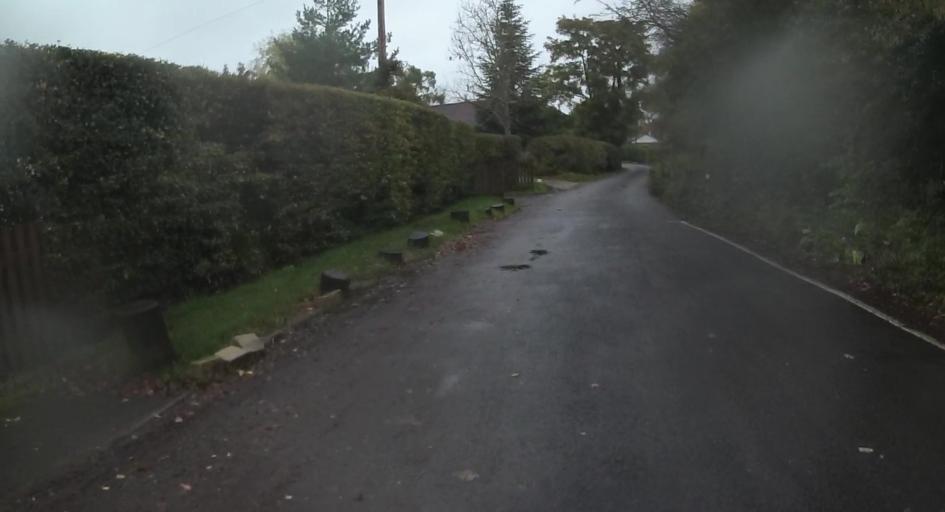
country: GB
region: England
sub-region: Hampshire
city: Kingsley
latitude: 51.1925
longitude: -0.8750
